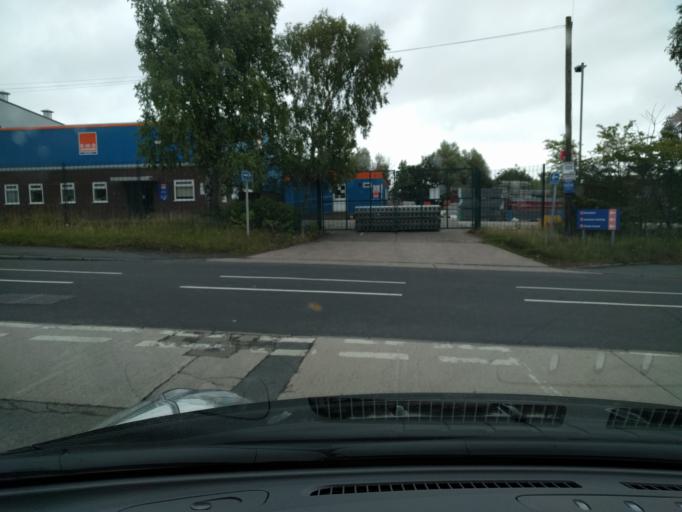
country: GB
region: England
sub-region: Borough of Wigan
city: Ashton in Makerfield
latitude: 53.4775
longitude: -2.6600
